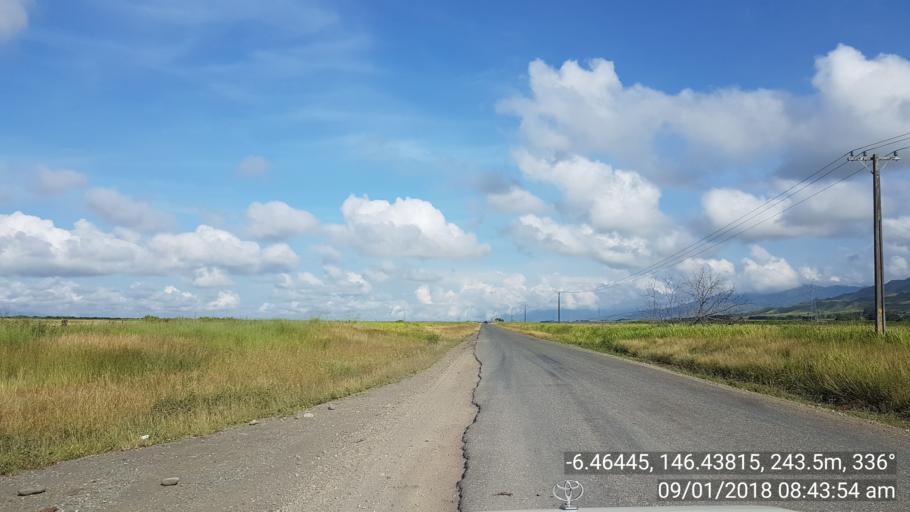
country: PG
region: Eastern Highlands
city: Kainantu
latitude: -6.4646
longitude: 146.4376
